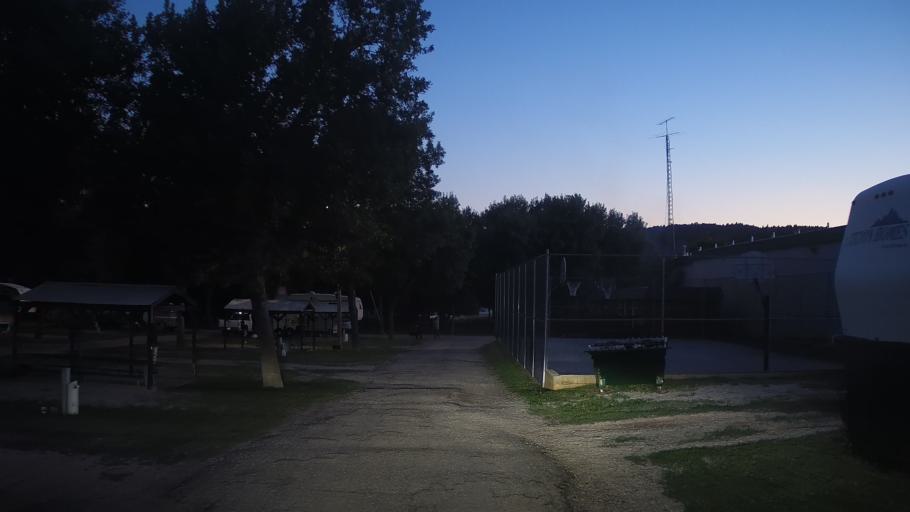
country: US
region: South Dakota
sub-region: Pennington County
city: Colonial Pine Hills
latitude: 43.9903
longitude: -103.2689
